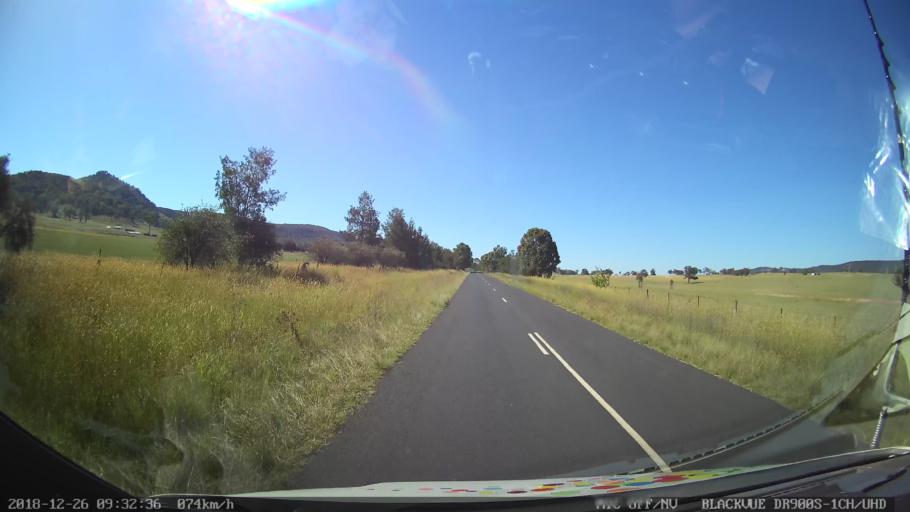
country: AU
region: New South Wales
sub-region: Mid-Western Regional
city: Kandos
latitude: -32.8861
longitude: 150.0327
